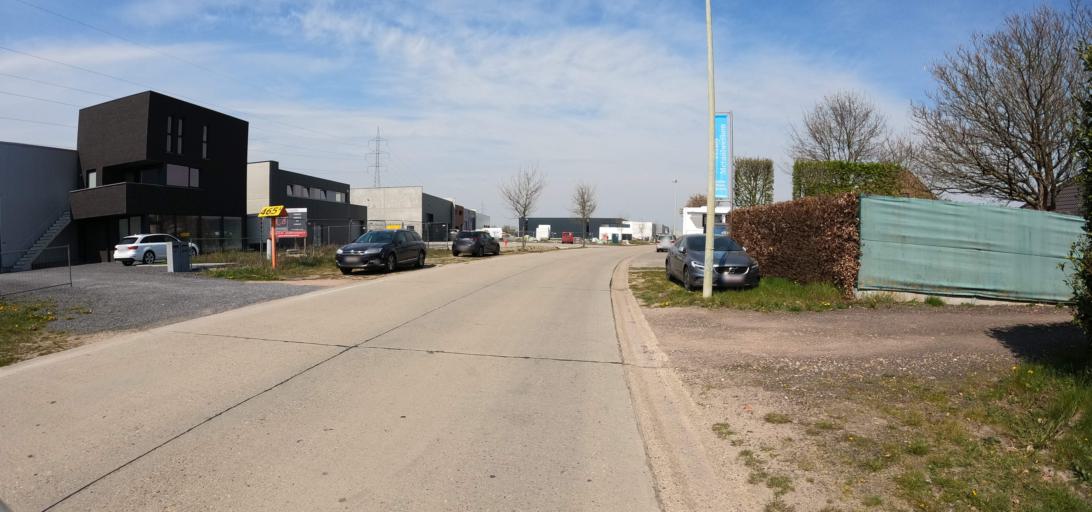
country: BE
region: Flanders
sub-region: Provincie Antwerpen
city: Beerse
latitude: 51.2996
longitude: 4.8306
